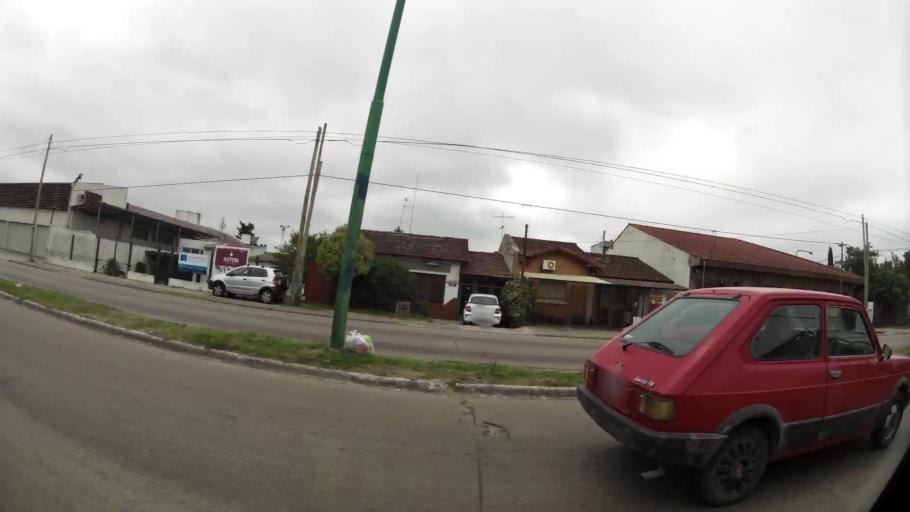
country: AR
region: Buenos Aires
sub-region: Partido de La Plata
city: La Plata
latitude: -34.9498
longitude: -57.9980
